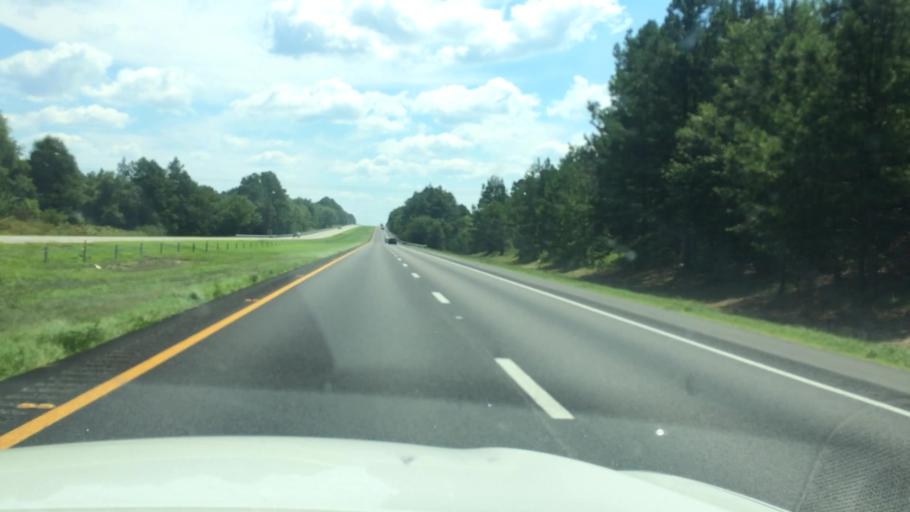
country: US
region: South Carolina
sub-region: Aiken County
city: Graniteville
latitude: 33.6340
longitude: -81.7781
